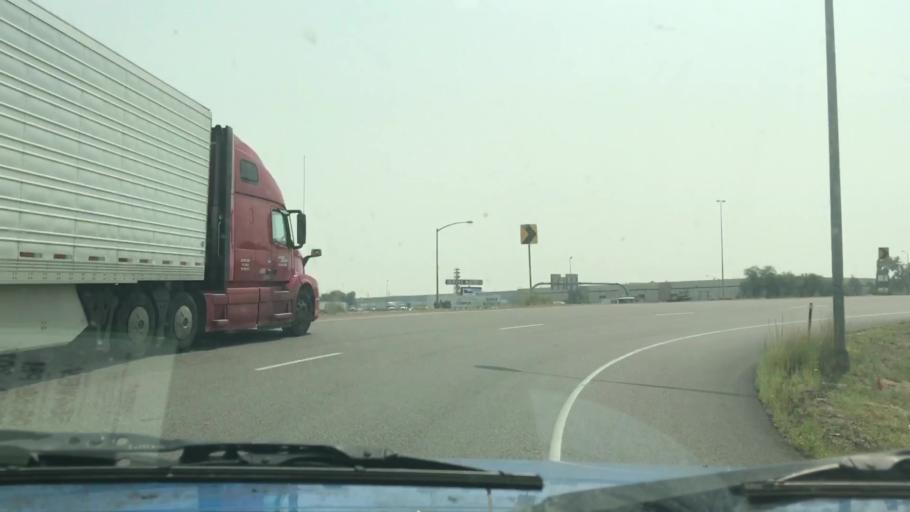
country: US
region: Colorado
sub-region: Adams County
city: Aurora
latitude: 39.7766
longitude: -104.8638
